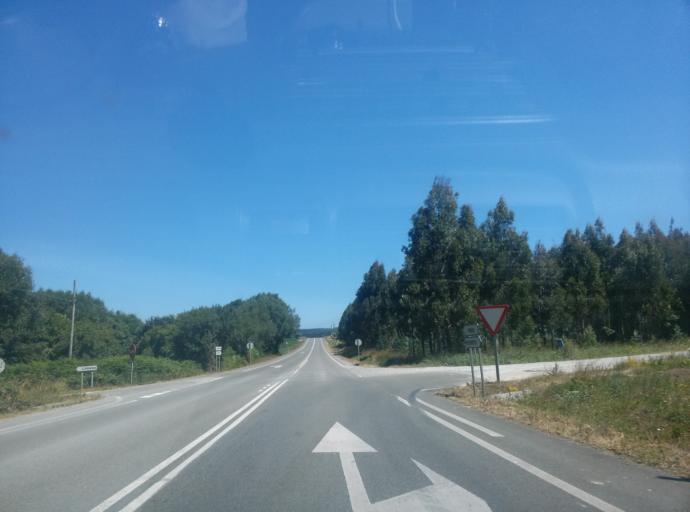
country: ES
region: Galicia
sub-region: Provincia de Lugo
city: Castro de Rei
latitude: 43.2368
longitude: -7.4044
